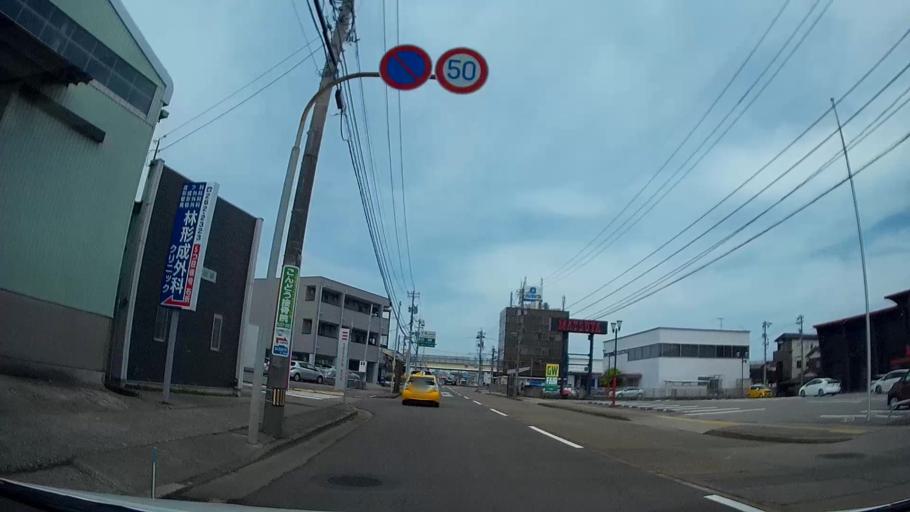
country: JP
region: Ishikawa
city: Kanazawa-shi
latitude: 36.5951
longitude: 136.6414
